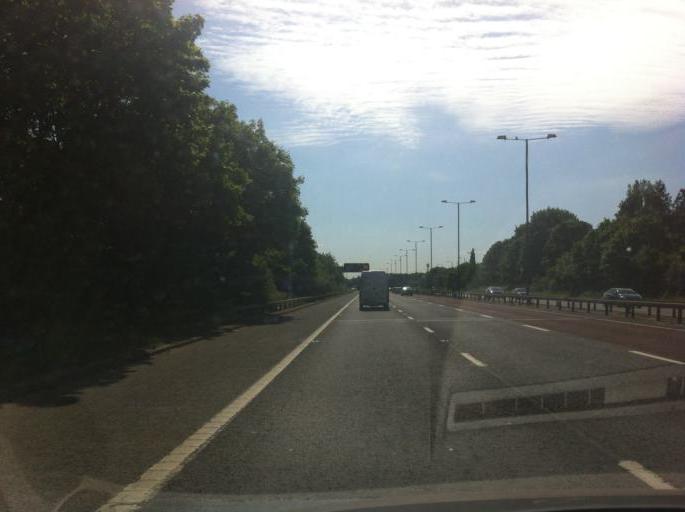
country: GB
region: England
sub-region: Greater London
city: Hayes
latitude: 51.4907
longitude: -0.4018
